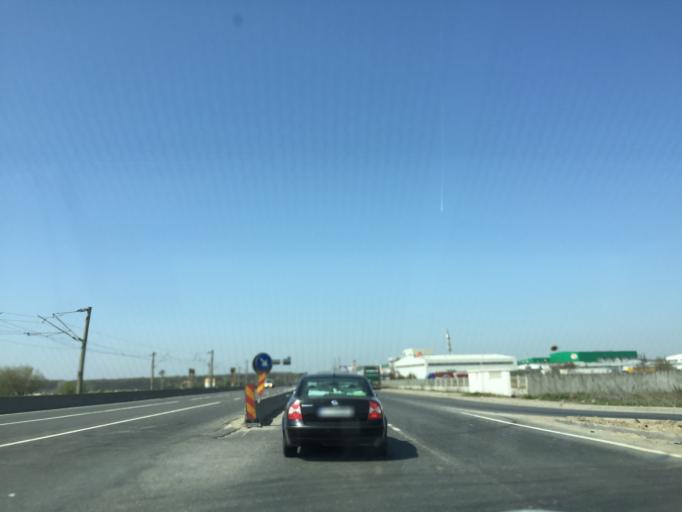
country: RO
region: Ilfov
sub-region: Comuna Tunari
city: Tunari
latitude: 44.5361
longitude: 26.1404
